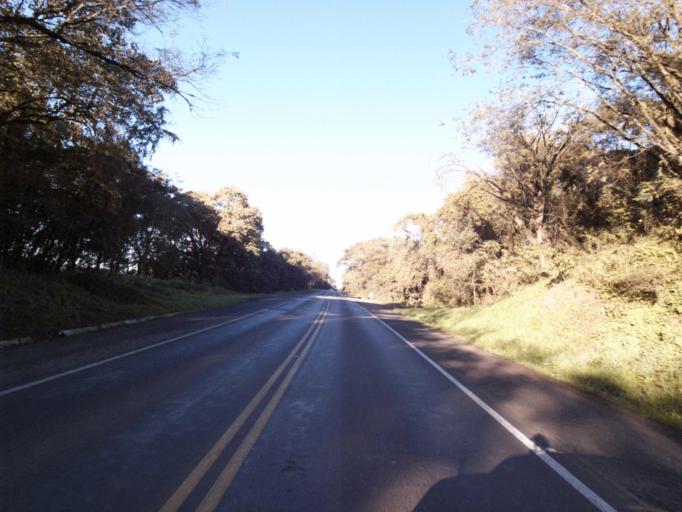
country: BR
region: Santa Catarina
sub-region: Sao Lourenco Do Oeste
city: Sao Lourenco dOeste
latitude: -26.7705
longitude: -53.2689
